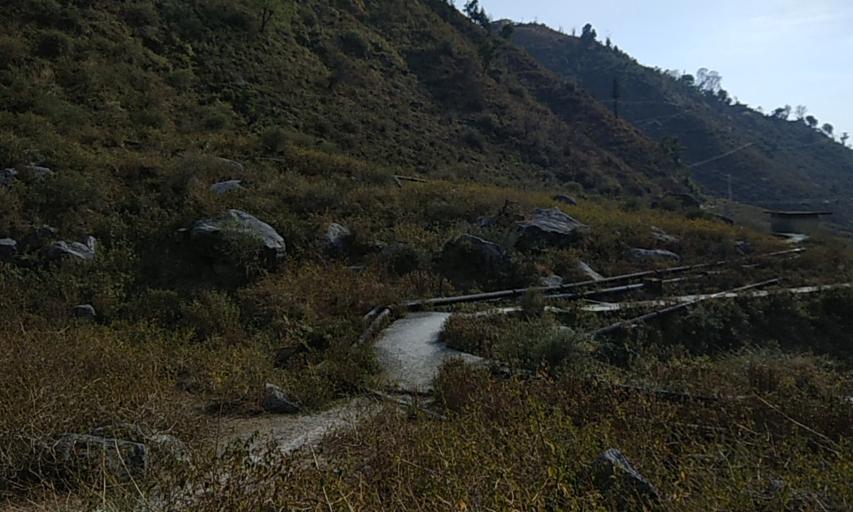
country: IN
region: Himachal Pradesh
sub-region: Kangra
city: Palampur
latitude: 32.1487
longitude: 76.5438
